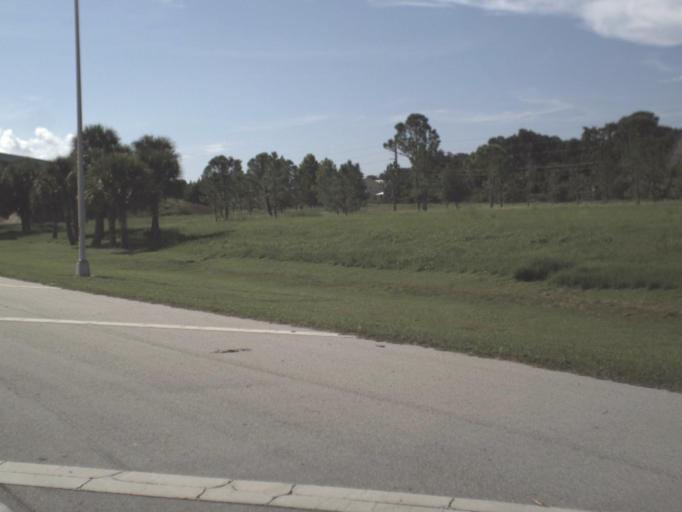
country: US
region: Florida
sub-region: Sarasota County
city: Laurel
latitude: 27.1497
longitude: -82.4643
